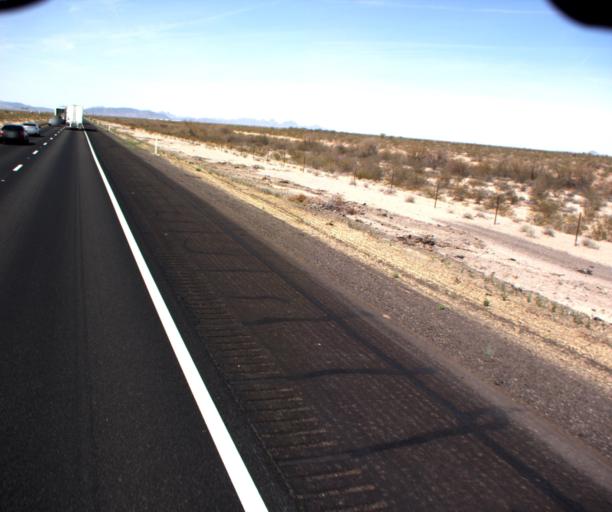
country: US
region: Arizona
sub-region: La Paz County
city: Salome
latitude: 33.6197
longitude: -113.6894
